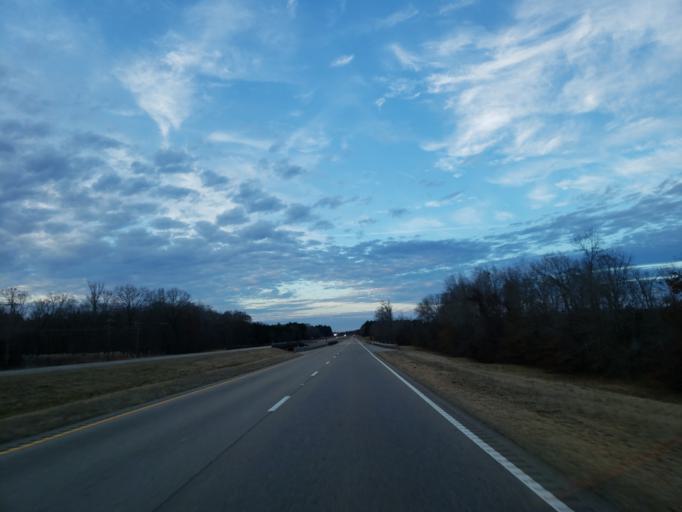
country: US
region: Mississippi
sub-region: Kemper County
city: De Kalb
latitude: 32.8151
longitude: -88.4570
